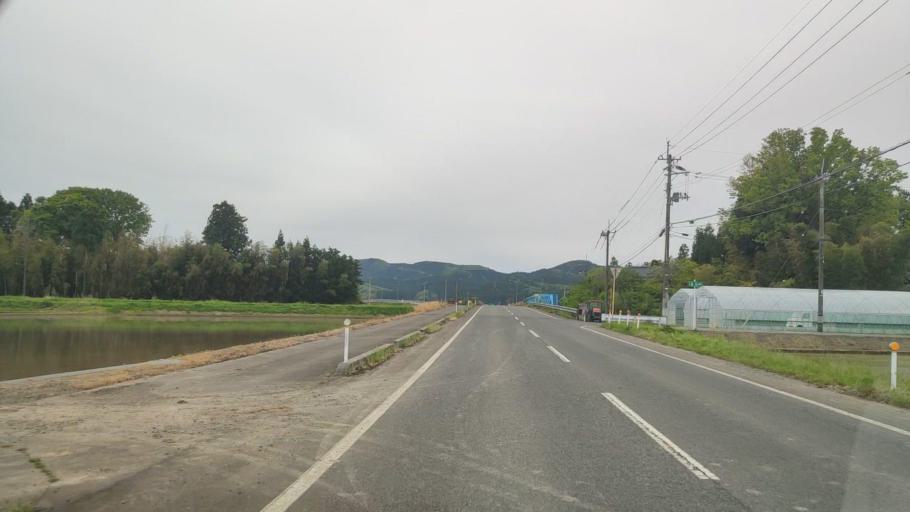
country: JP
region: Niigata
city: Gosen
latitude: 37.7292
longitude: 139.1575
